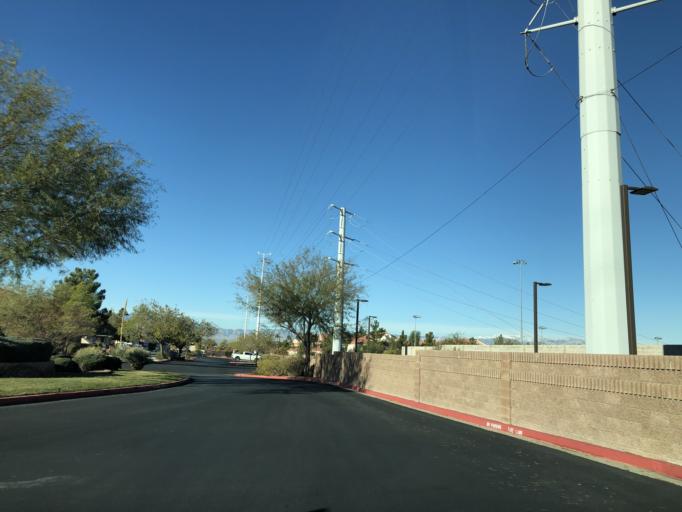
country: US
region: Nevada
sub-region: Clark County
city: Whitney
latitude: 36.0023
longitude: -115.0905
